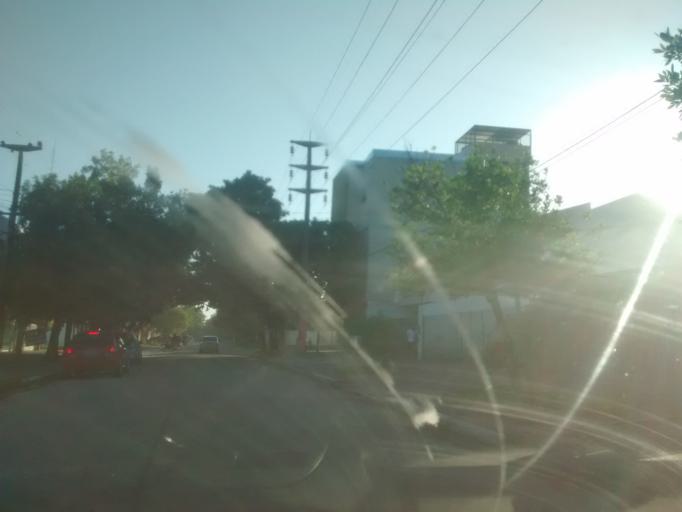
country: AR
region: Chaco
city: Resistencia
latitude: -27.4618
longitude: -58.9932
